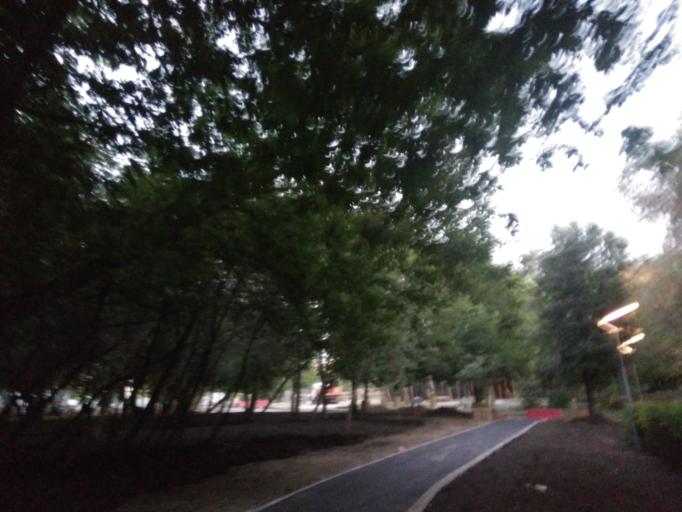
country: RU
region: Moskovskaya
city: Levoberezhnaya
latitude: 55.8775
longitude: 37.4675
